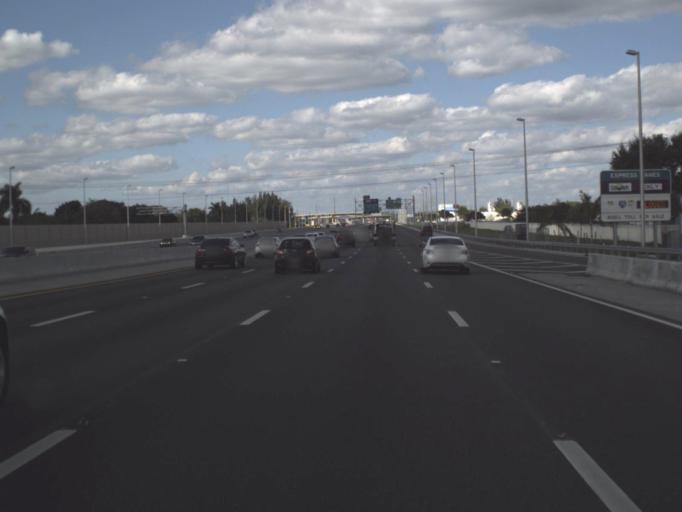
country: US
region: Florida
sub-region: Broward County
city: Davie
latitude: 26.0689
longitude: -80.2154
